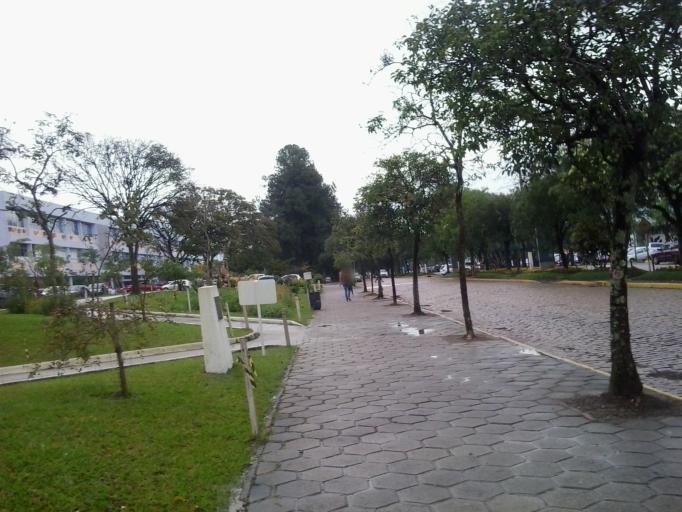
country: BR
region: Rio Grande do Sul
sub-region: Santa Maria
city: Santa Maria
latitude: -29.7146
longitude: -53.7160
